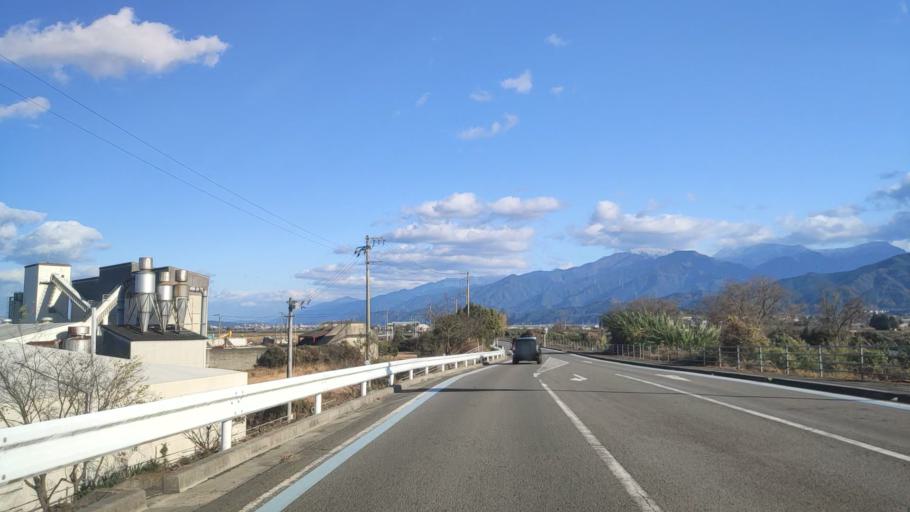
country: JP
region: Ehime
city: Saijo
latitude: 33.9068
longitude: 133.1127
